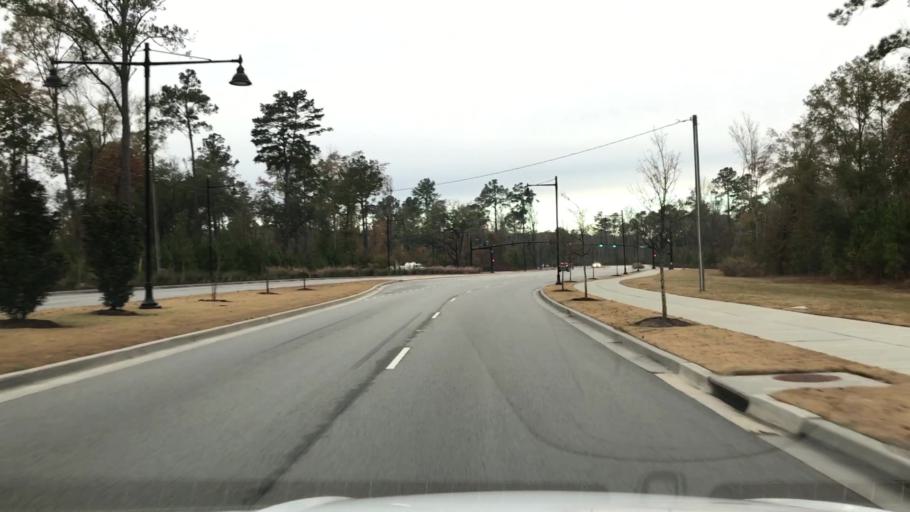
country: US
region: South Carolina
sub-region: Berkeley County
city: Ladson
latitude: 32.9605
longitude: -80.0793
